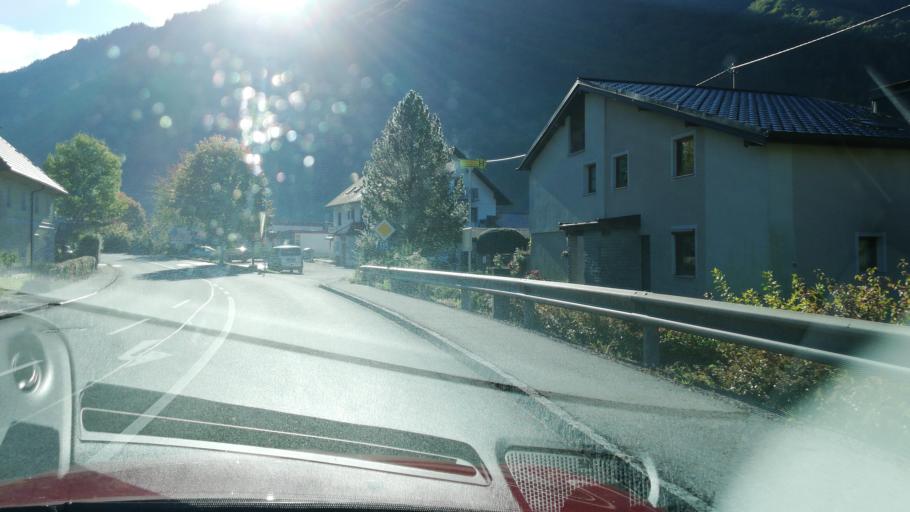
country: AT
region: Upper Austria
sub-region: Politischer Bezirk Steyr-Land
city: Reichraming
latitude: 47.8935
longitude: 14.4620
